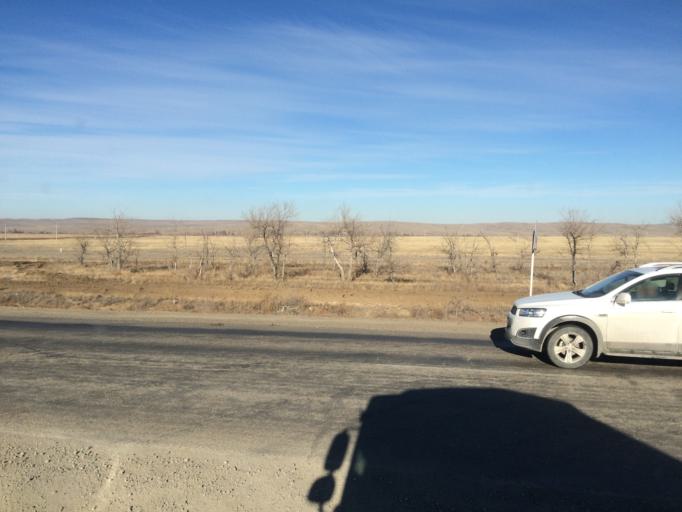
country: KZ
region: Aqtoebe
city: Aqtobe
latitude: 50.2928
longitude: 57.6245
